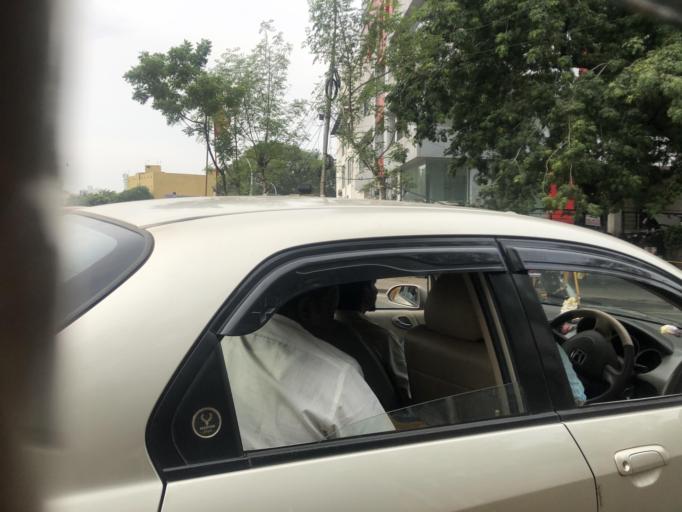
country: IN
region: Tamil Nadu
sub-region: Chennai
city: Chennai
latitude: 13.0682
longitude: 80.2695
